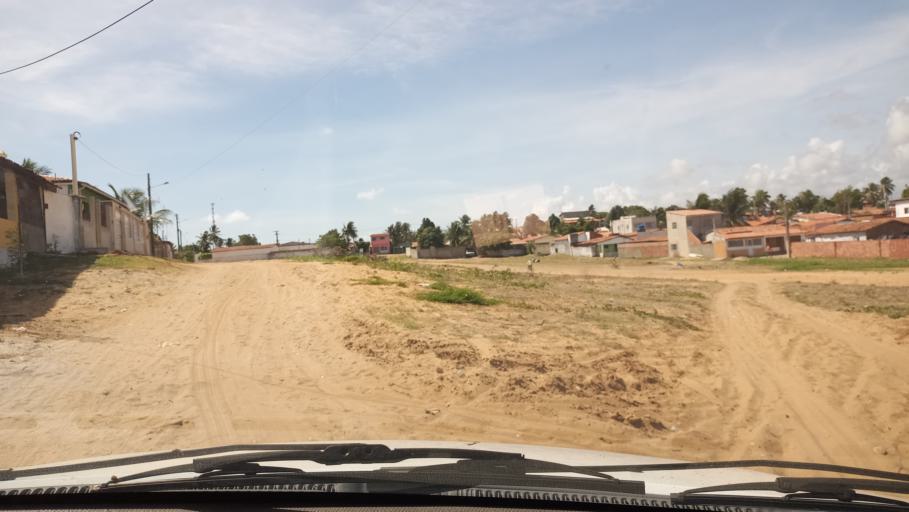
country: BR
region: Rio Grande do Norte
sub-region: Maxaranguape
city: Sao Miguel
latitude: -5.5162
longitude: -35.2632
